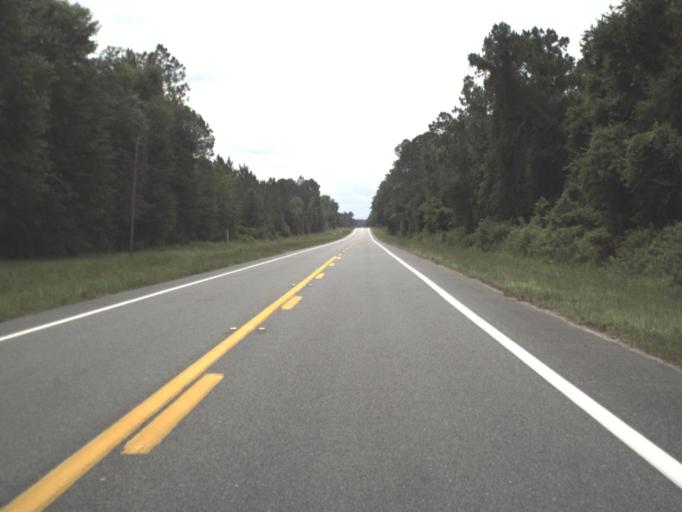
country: US
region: Florida
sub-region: Union County
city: Lake Butler
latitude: 30.0795
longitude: -82.4508
